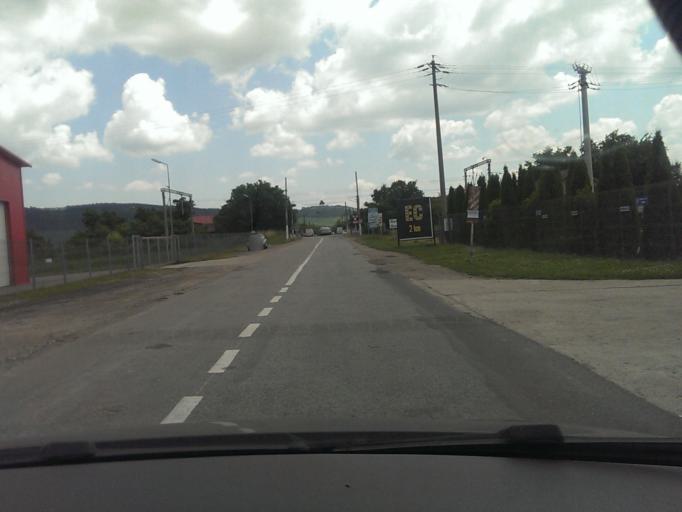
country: RO
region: Cluj
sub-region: Comuna Bontida
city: Rascruci
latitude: 46.9275
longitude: 23.7851
